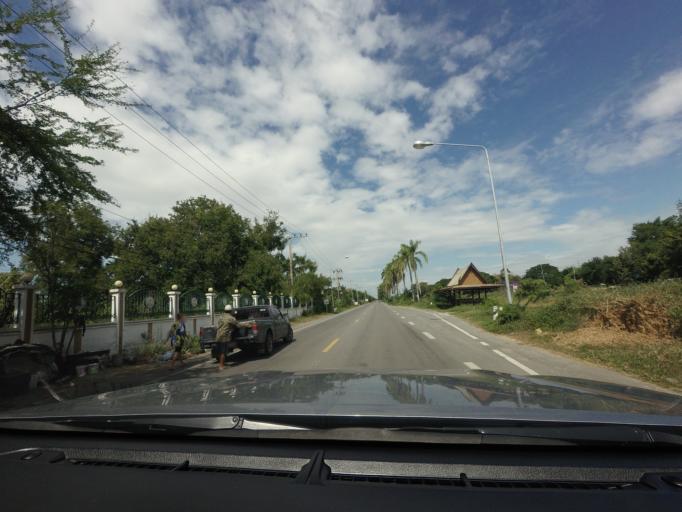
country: TH
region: Suphan Buri
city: Suphan Buri
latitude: 14.4767
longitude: 100.0914
